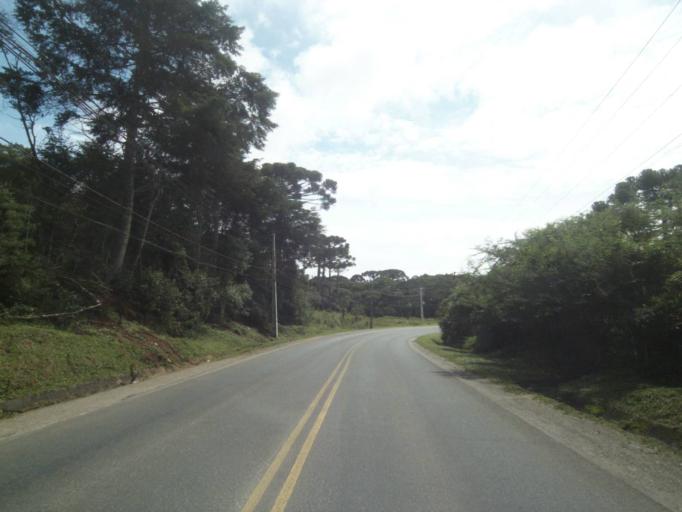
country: BR
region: Parana
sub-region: Campina Grande Do Sul
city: Campina Grande do Sul
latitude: -25.3097
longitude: -49.0658
